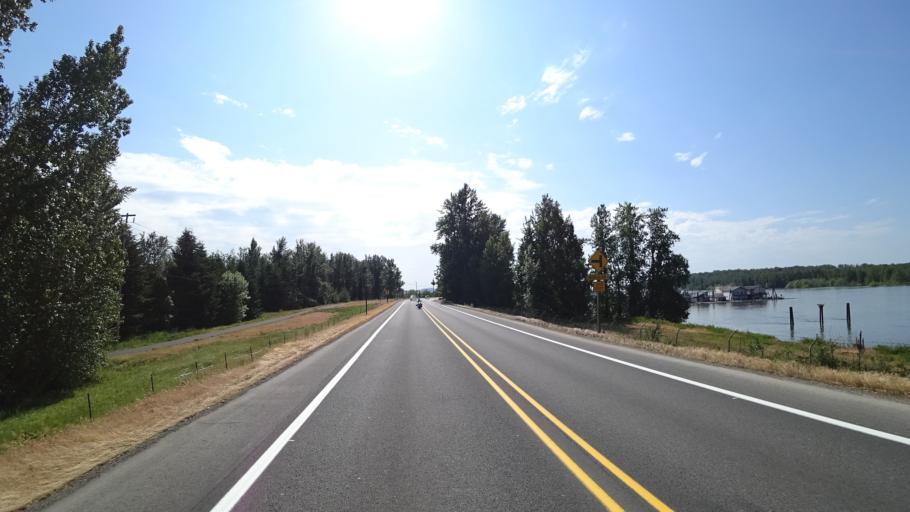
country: US
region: Oregon
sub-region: Multnomah County
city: Fairview
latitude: 45.5578
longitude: -122.4579
